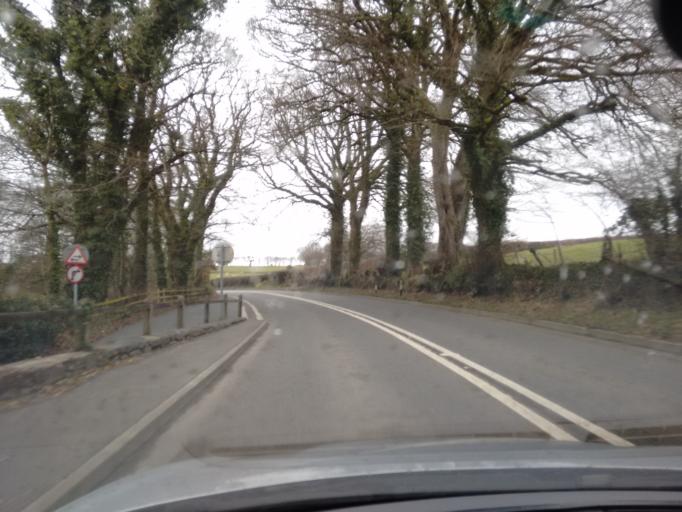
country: GB
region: England
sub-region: Devon
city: Okehampton
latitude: 50.7321
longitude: -4.0116
